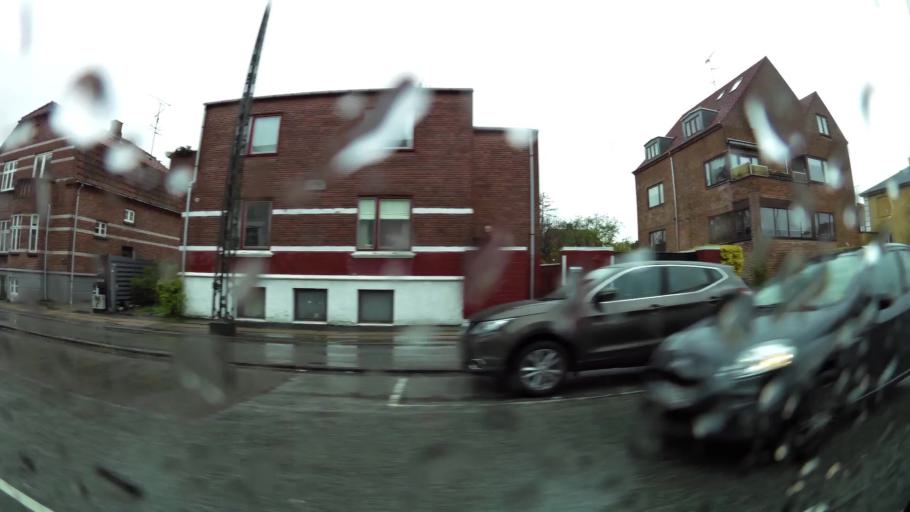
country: DK
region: Capital Region
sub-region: Kobenhavn
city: Vanlose
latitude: 55.6920
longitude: 12.4807
